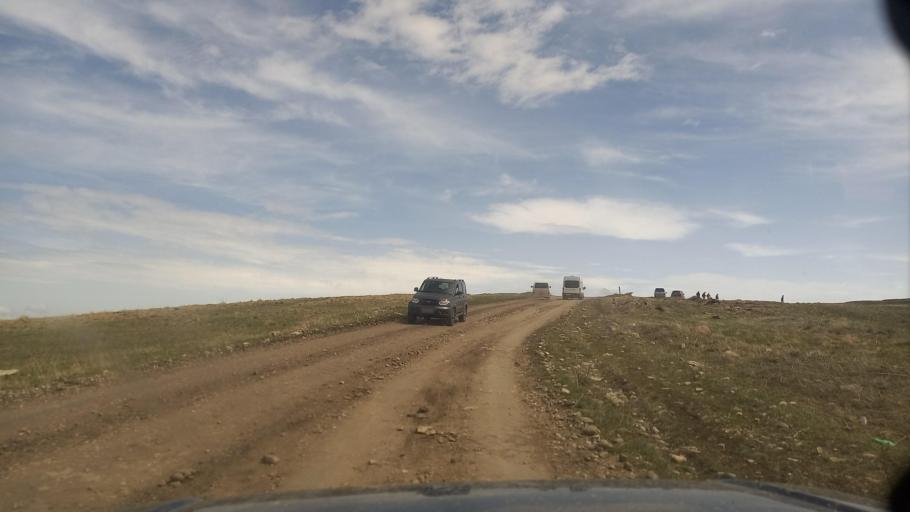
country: RU
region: Stavropol'skiy
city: Kislovodsk
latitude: 43.7438
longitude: 42.6785
